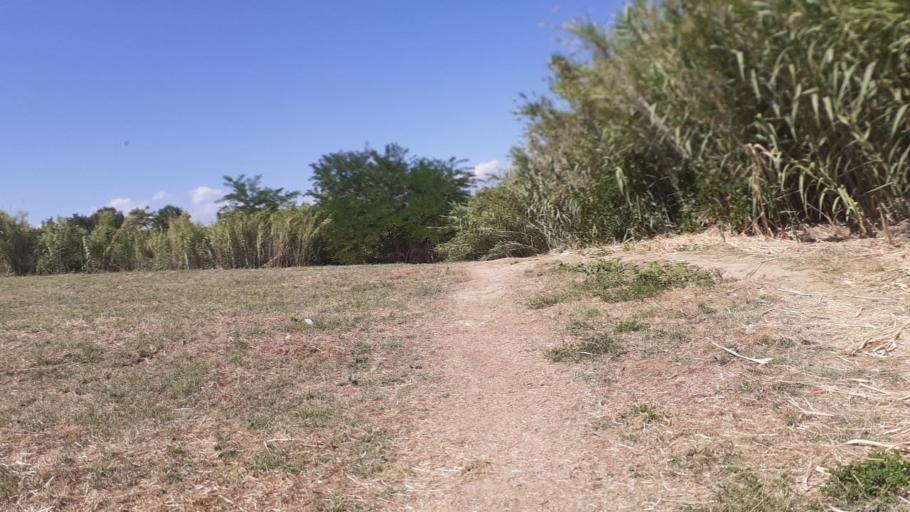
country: IT
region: Abruzzo
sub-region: Provincia di Chieti
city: Torino di Sangro
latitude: 42.2191
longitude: 14.5731
